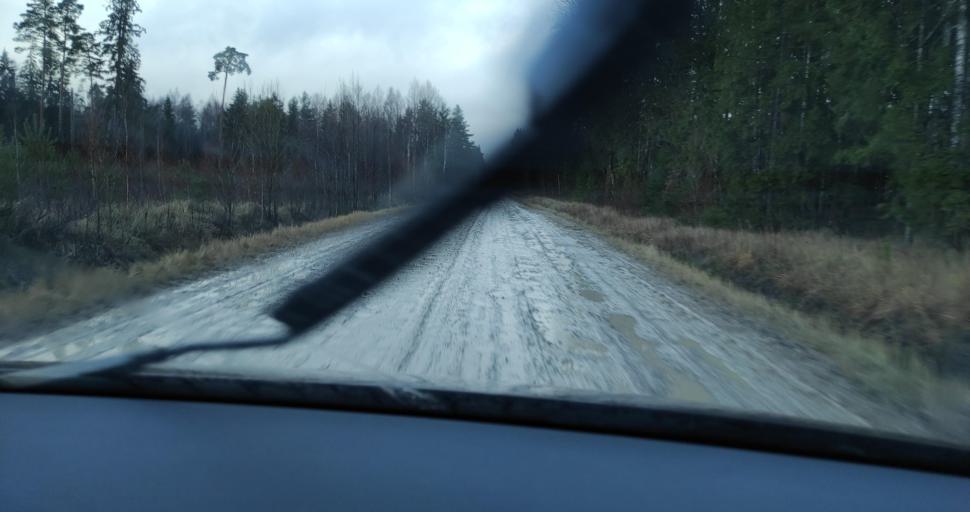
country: LV
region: Skrunda
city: Skrunda
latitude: 56.7236
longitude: 22.2025
